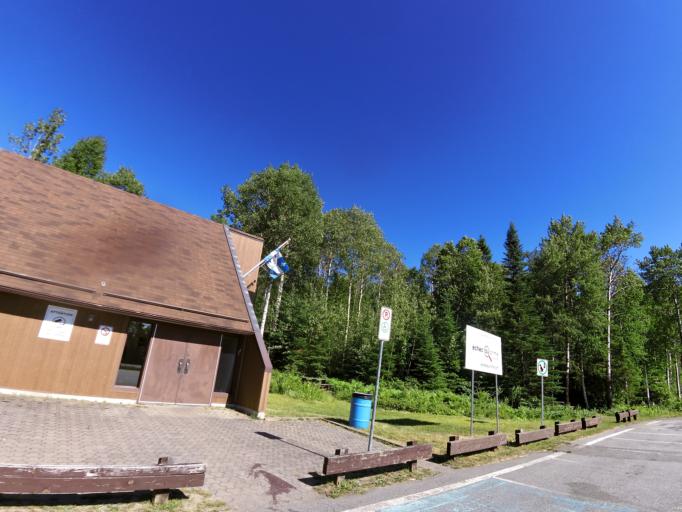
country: CA
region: Quebec
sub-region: Abitibi-Temiscamingue
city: Senneterre
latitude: 47.9987
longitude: -77.3595
